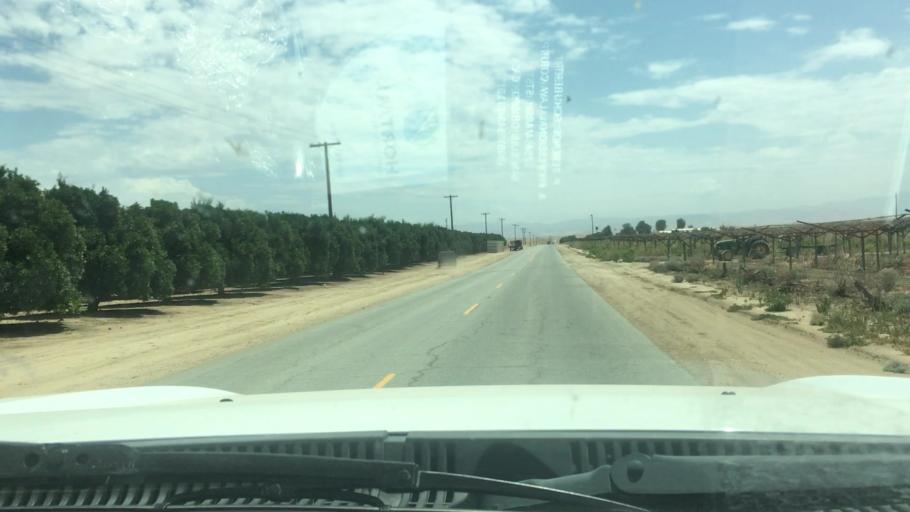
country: US
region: California
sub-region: Kern County
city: McFarland
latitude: 35.6024
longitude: -119.1023
